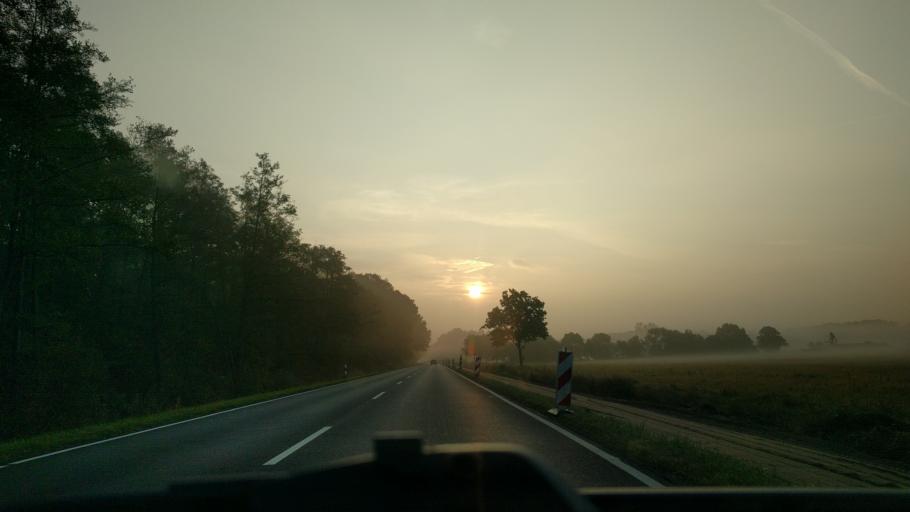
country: DE
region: Lower Saxony
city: Calberlah
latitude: 52.4323
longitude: 10.6325
